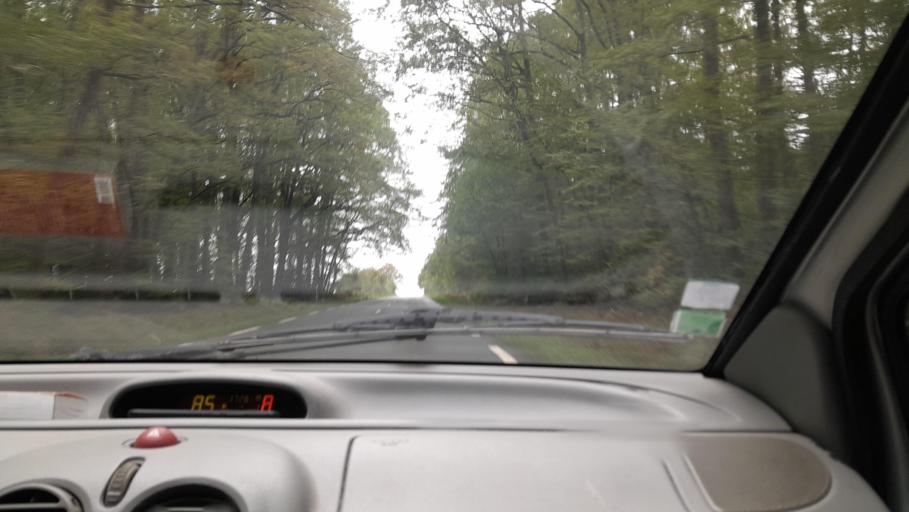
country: FR
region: Pays de la Loire
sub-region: Departement de Maine-et-Loire
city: Pouance
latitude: 47.6912
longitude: -1.1851
